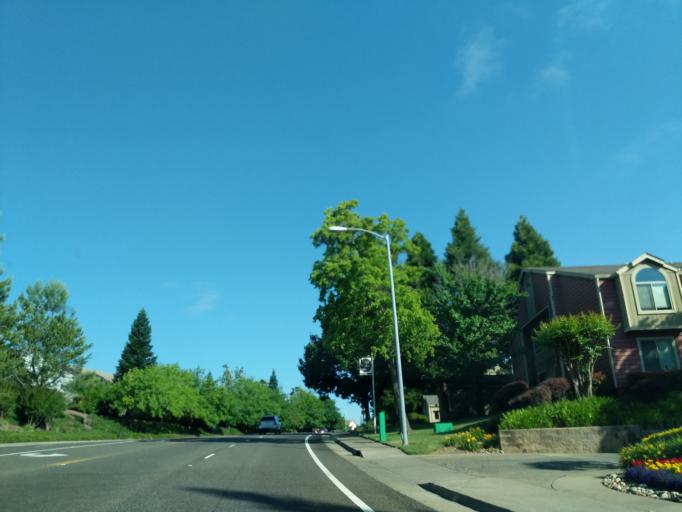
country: US
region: California
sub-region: Sacramento County
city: Folsom
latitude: 38.6623
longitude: -121.1593
